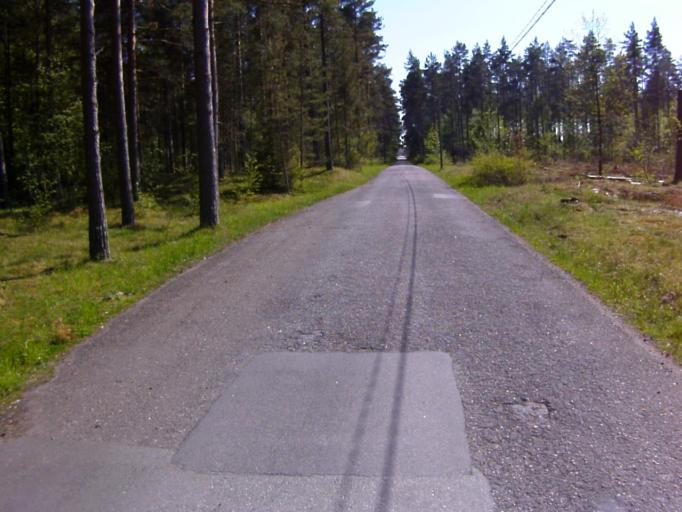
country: SE
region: Skane
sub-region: Kristianstads Kommun
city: Degeberga
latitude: 55.9050
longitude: 14.0926
